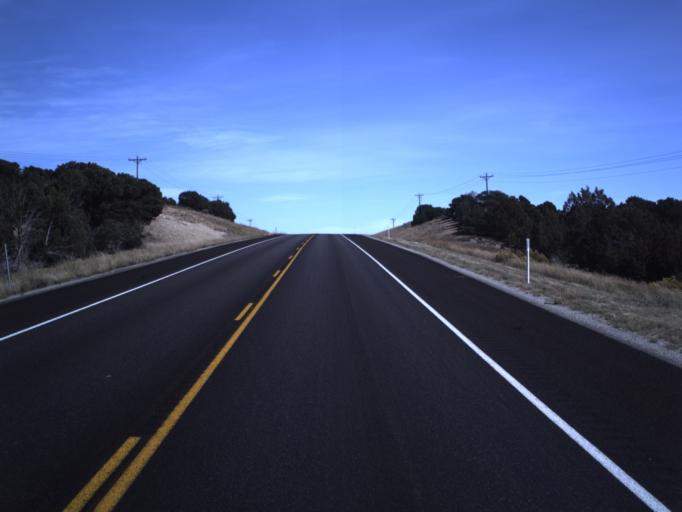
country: US
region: Utah
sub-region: San Juan County
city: Monticello
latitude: 37.8728
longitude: -109.2973
